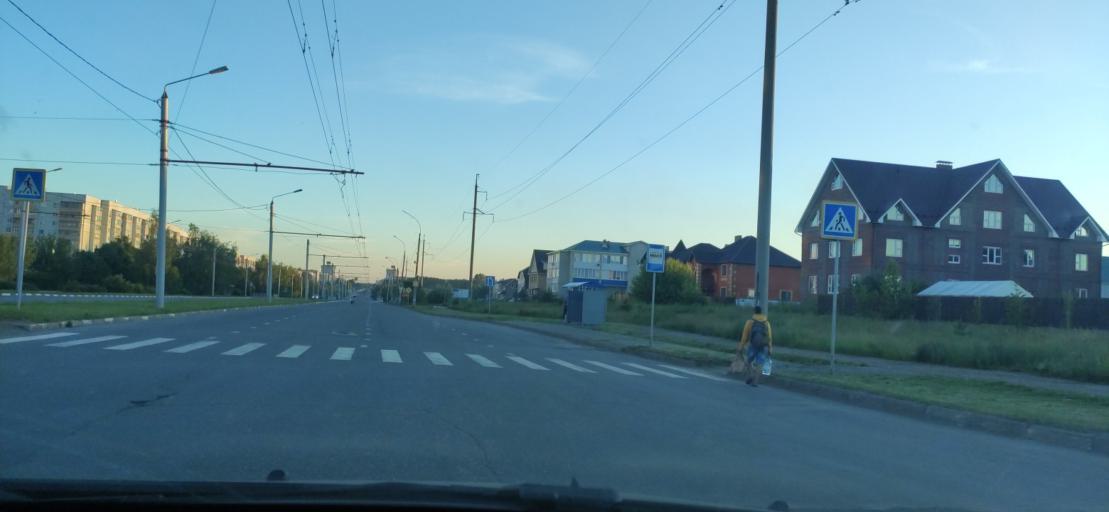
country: RU
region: Ulyanovsk
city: Mirnyy
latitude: 54.3887
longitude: 48.6115
